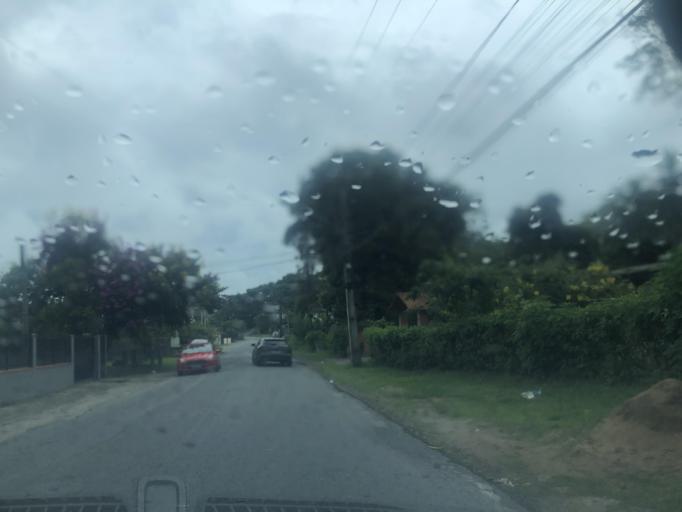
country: BR
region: Santa Catarina
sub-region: Sao Francisco Do Sul
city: Sao Francisco do Sul
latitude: -26.2373
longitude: -48.6145
